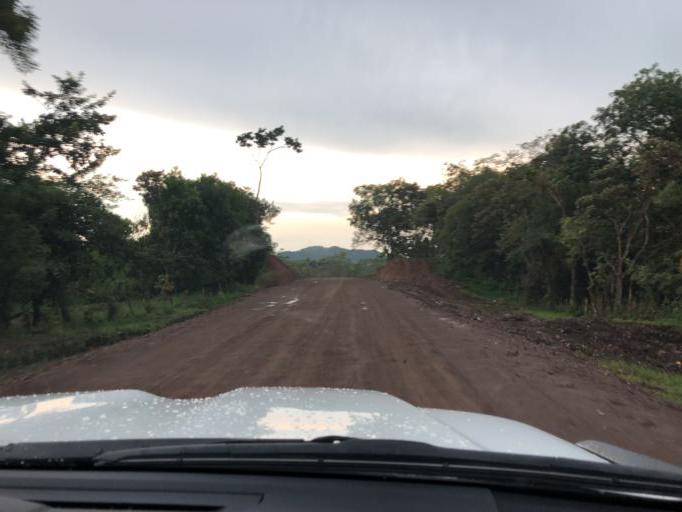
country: NI
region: Chontales
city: La Libertad
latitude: 12.1978
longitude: -85.1774
